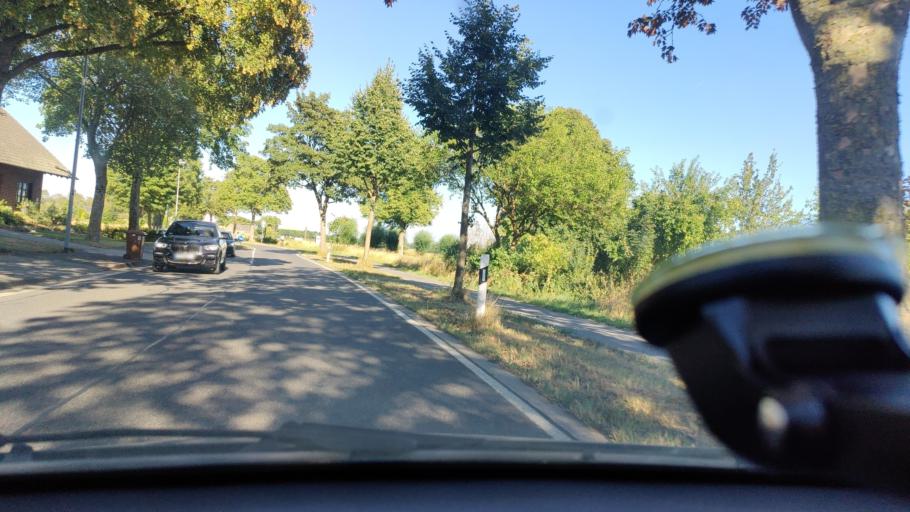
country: DE
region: North Rhine-Westphalia
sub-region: Regierungsbezirk Dusseldorf
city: Kleve
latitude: 51.7887
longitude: 6.1627
